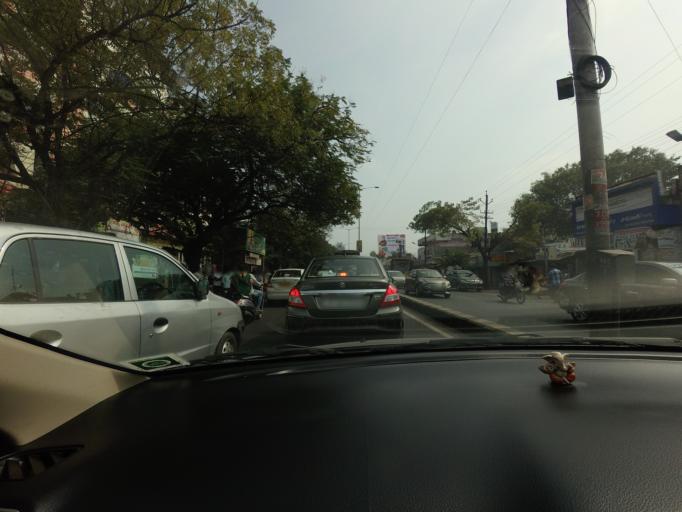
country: IN
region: Andhra Pradesh
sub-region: Krishna
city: Yanamalakuduru
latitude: 16.4931
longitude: 80.6652
